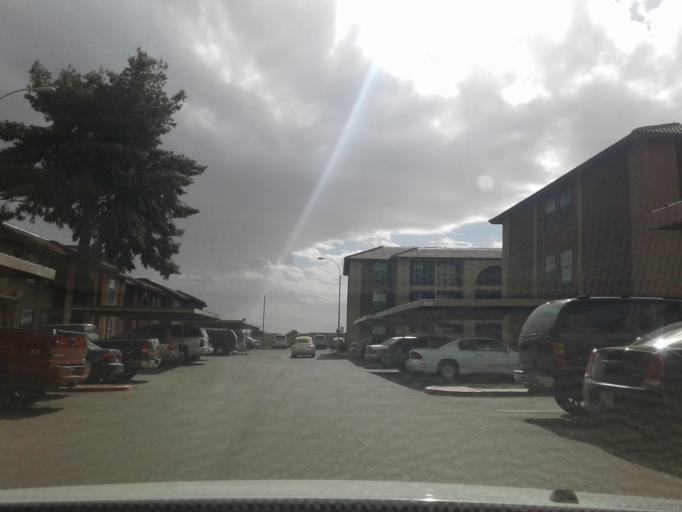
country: US
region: Arizona
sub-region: Maricopa County
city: Glendale
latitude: 33.4648
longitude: -112.1805
